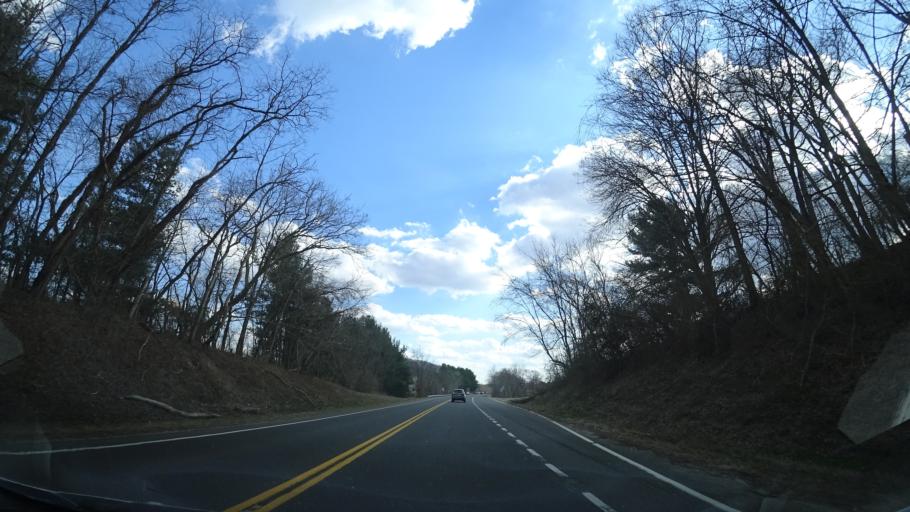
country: US
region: Virginia
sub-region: Warren County
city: Shenandoah Farms
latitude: 38.9854
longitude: -77.9488
